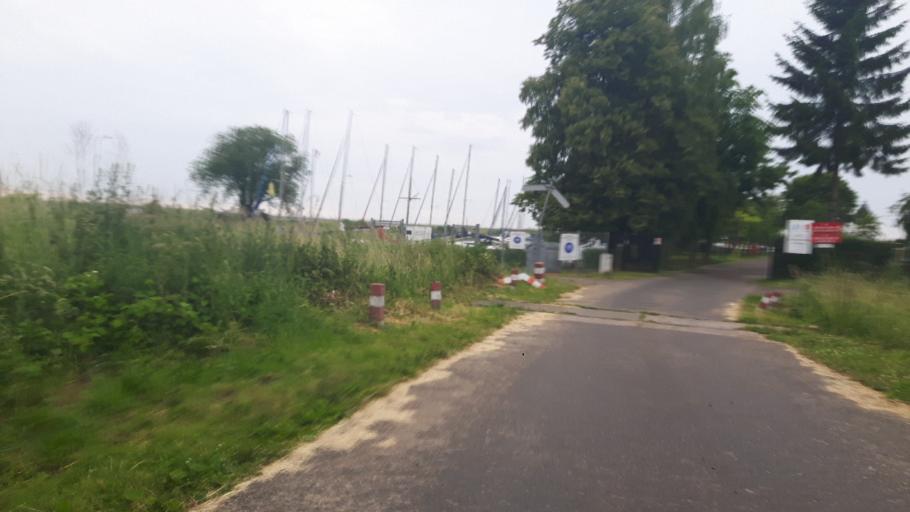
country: PL
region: Pomeranian Voivodeship
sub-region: Powiat nowodworski
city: Krynica Morska
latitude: 54.2724
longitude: 19.4165
